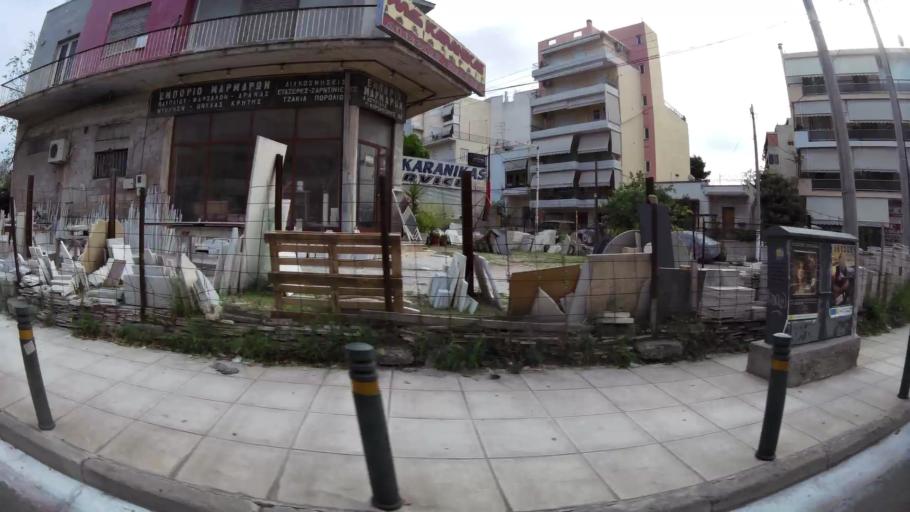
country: GR
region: Attica
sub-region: Nomarchia Athinas
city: Palaio Faliro
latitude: 37.9319
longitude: 23.7020
